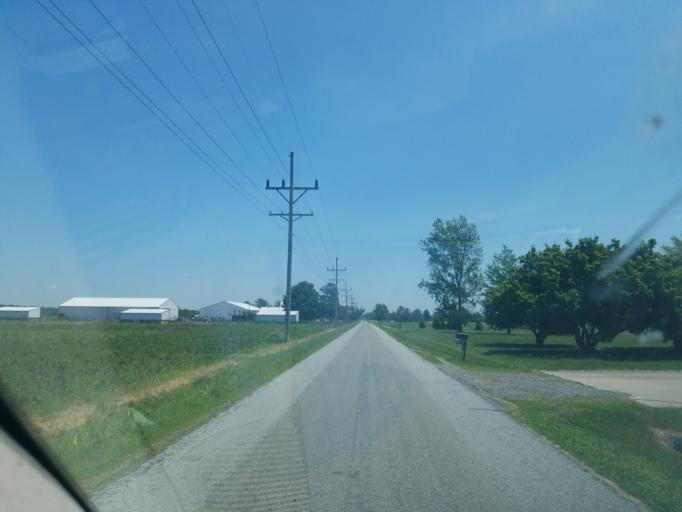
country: US
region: Ohio
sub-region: Allen County
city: Delphos
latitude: 40.7794
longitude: -84.3294
